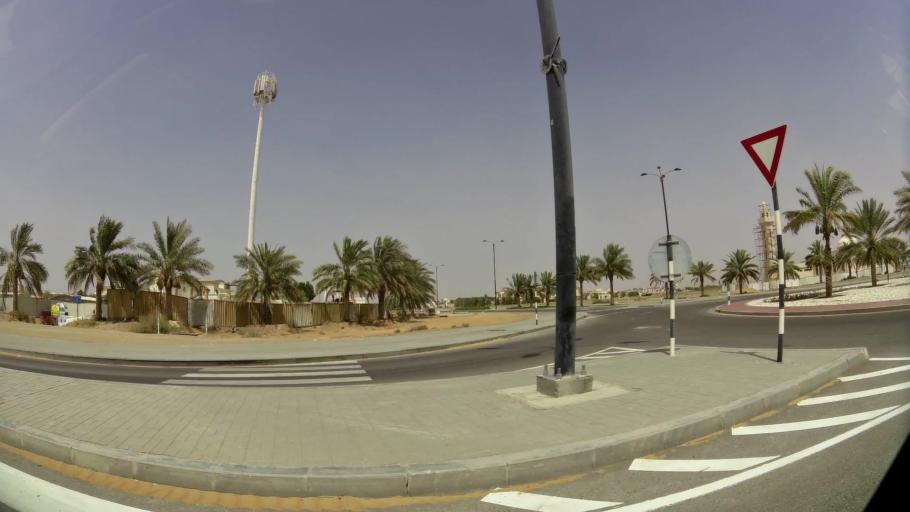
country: AE
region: Abu Dhabi
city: Al Ain
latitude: 24.1369
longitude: 55.6323
